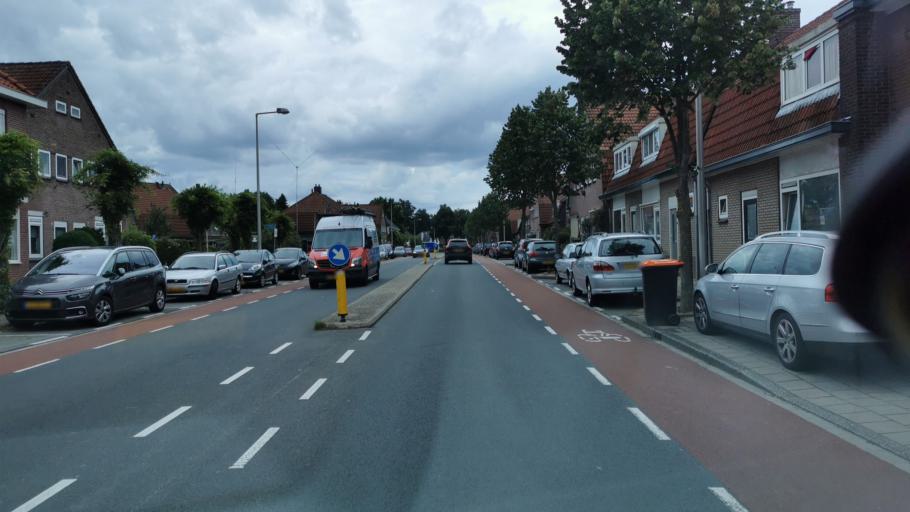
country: NL
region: Overijssel
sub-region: Gemeente Enschede
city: Enschede
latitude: 52.2296
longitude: 6.9038
